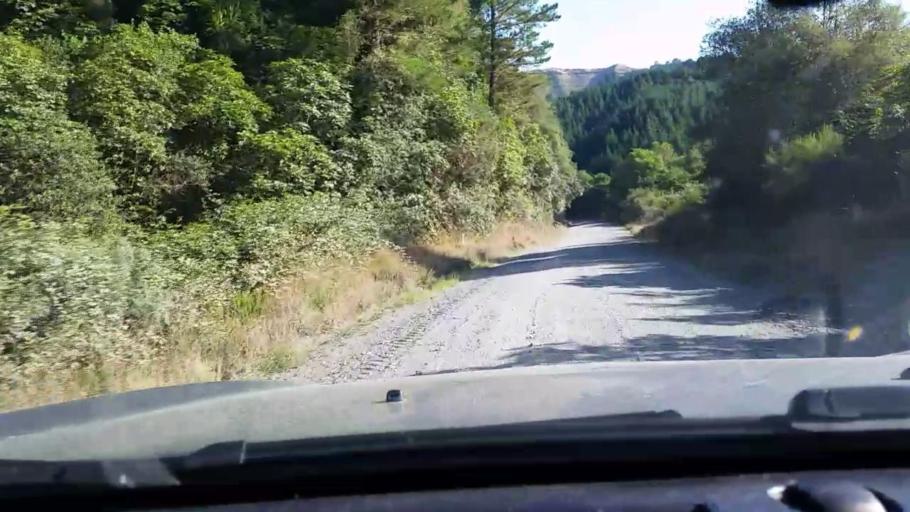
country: NZ
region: Waikato
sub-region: Taupo District
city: Taupo
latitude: -38.4670
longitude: 176.1612
